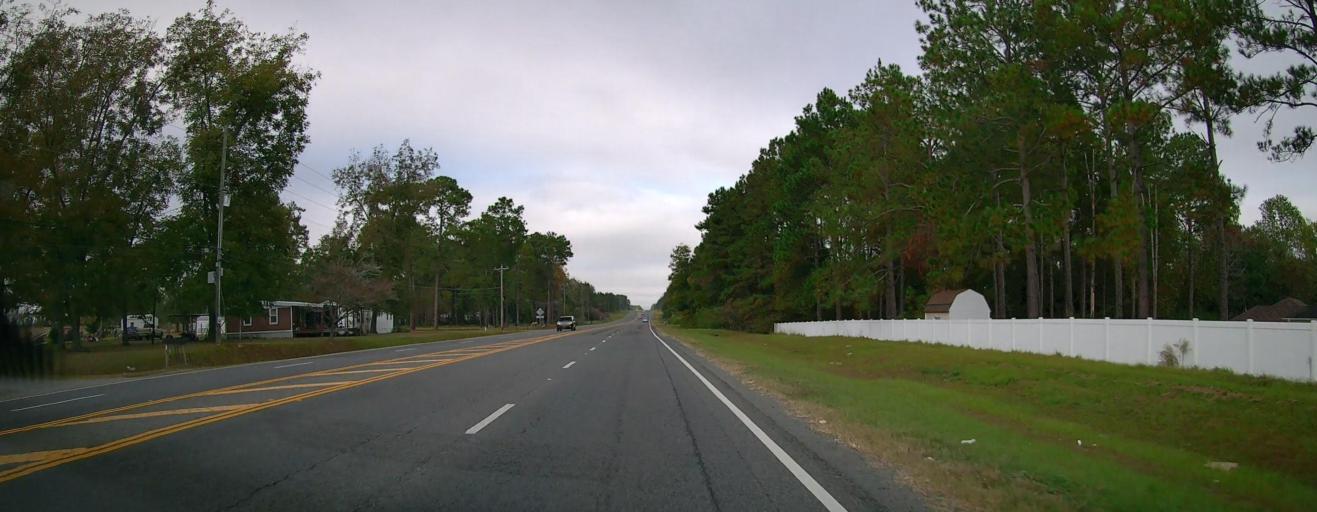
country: US
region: Georgia
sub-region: Tift County
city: Unionville
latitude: 31.4049
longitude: -83.5358
